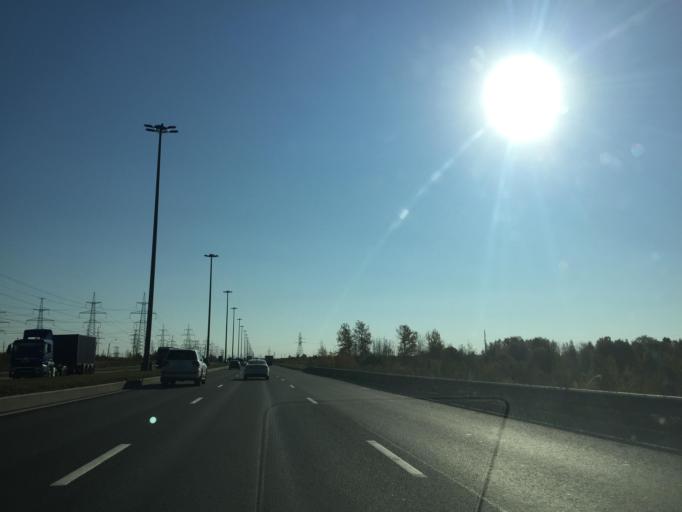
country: RU
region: St.-Petersburg
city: Petro-Slavyanka
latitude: 59.7625
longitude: 30.5082
